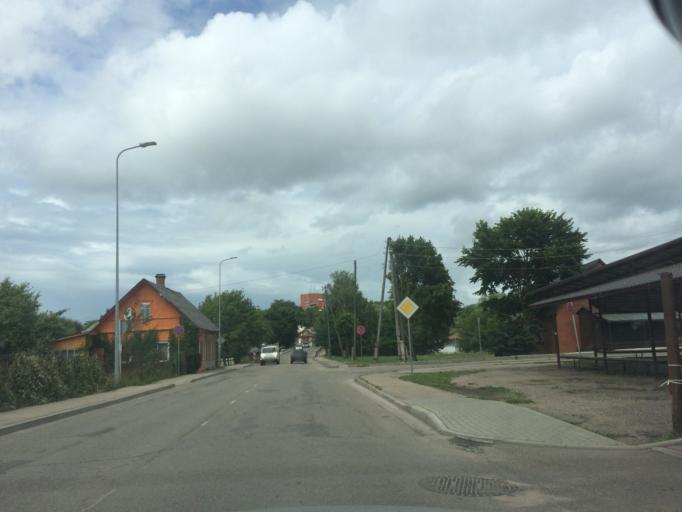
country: LV
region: Rezekne
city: Rezekne
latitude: 56.5004
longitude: 27.3329
